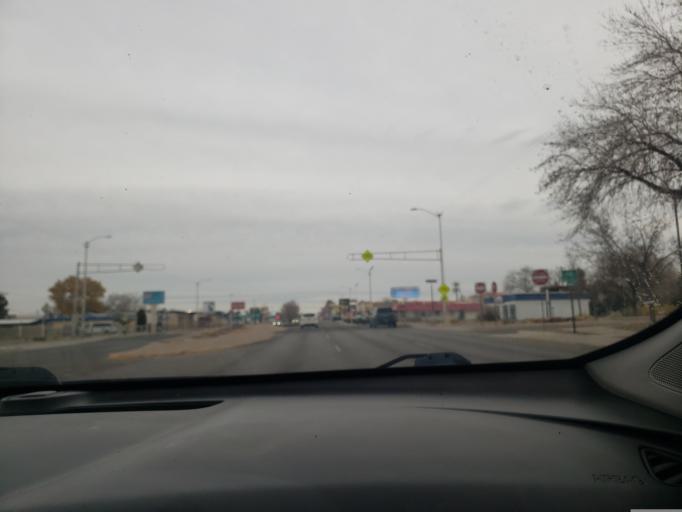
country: US
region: New Mexico
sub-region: Bernalillo County
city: North Valley
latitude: 35.1247
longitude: -106.5864
